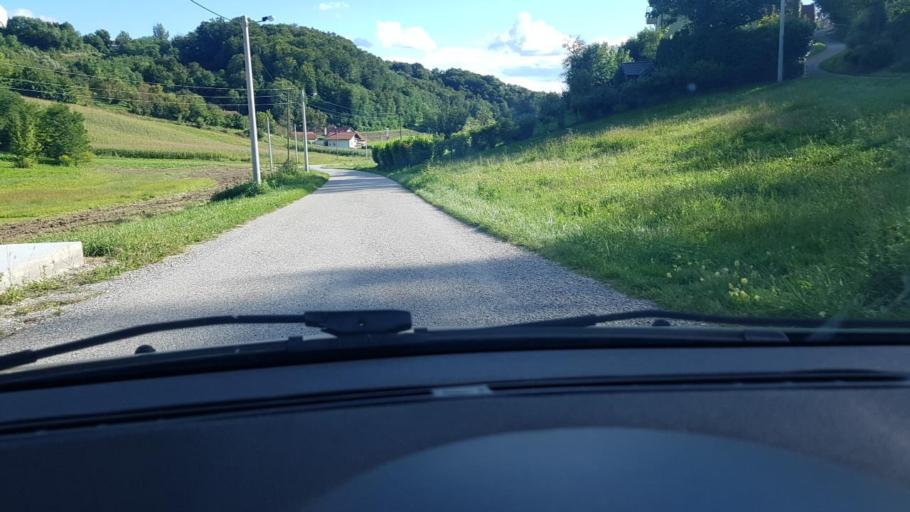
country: HR
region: Krapinsko-Zagorska
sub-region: Grad Krapina
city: Krapina
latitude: 46.1462
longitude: 15.8393
